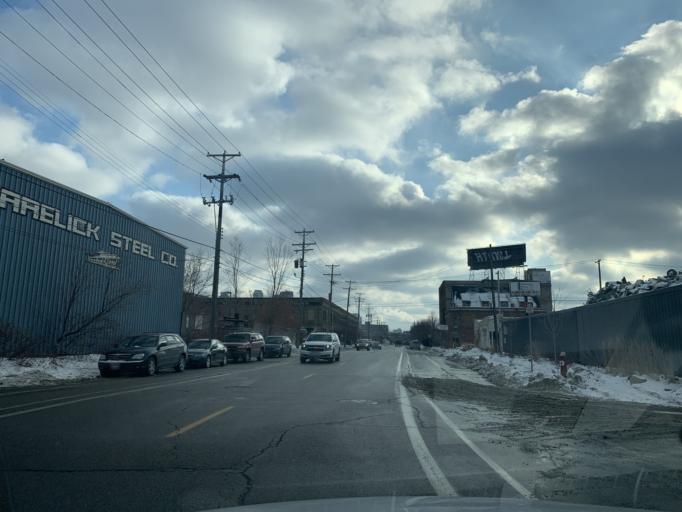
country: US
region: Minnesota
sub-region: Hennepin County
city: Minneapolis
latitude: 44.9983
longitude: -93.2800
